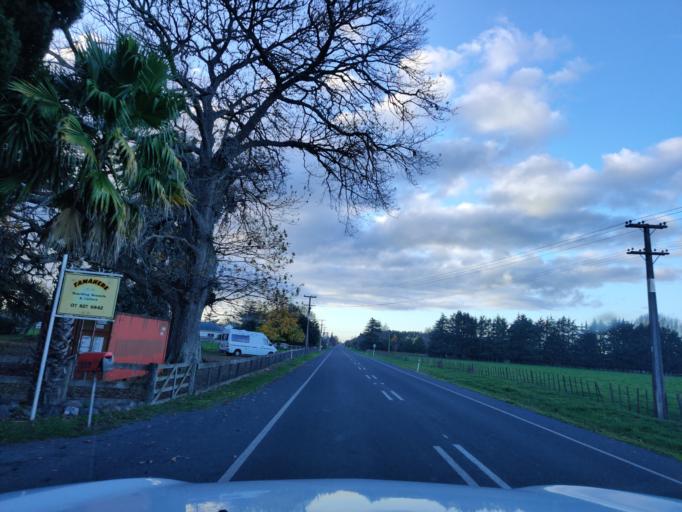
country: NZ
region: Waikato
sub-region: Waipa District
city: Cambridge
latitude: -37.8653
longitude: 175.4390
